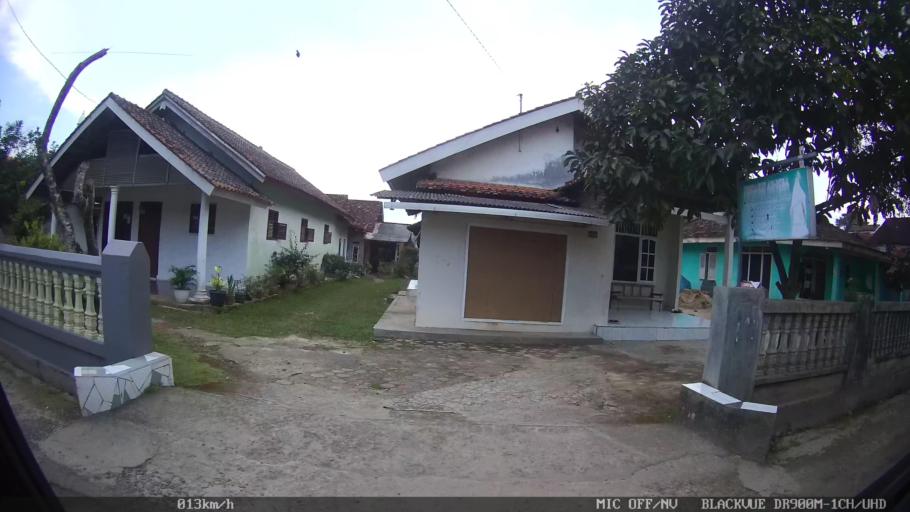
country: ID
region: Lampung
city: Kedaton
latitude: -5.4018
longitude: 105.2166
